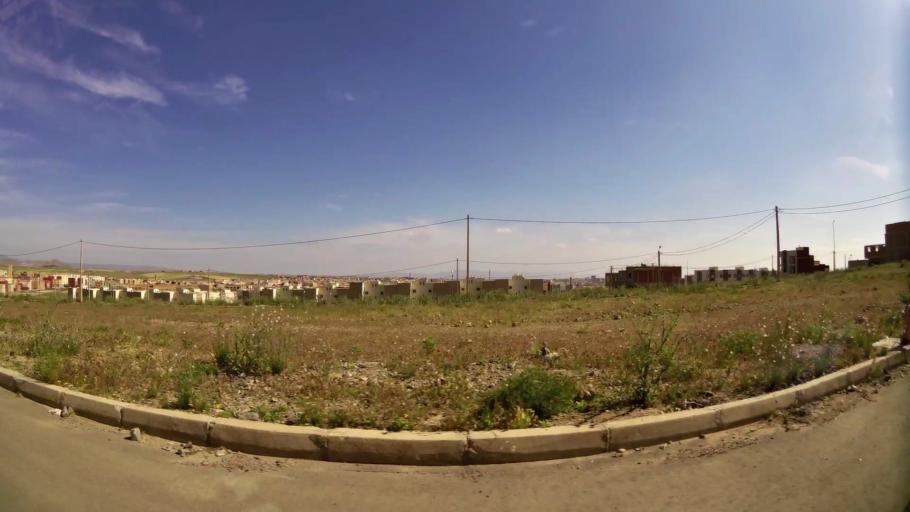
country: MA
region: Oriental
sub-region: Oujda-Angad
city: Oujda
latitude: 34.6534
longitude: -1.9446
